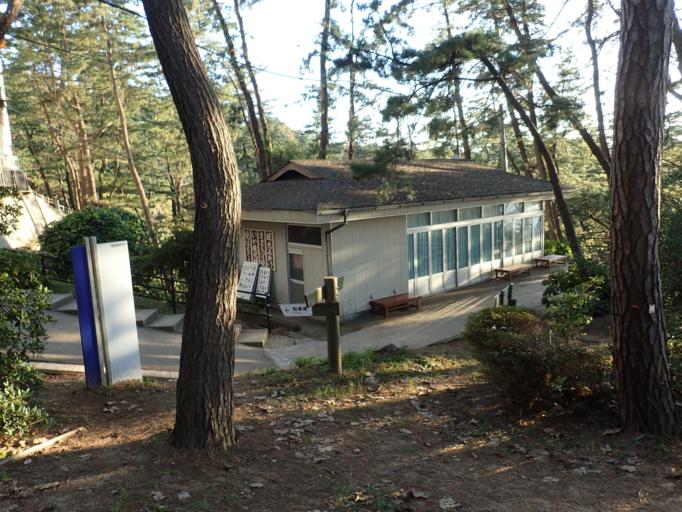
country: JP
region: Ishikawa
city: Hakui
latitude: 37.0948
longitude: 136.7274
